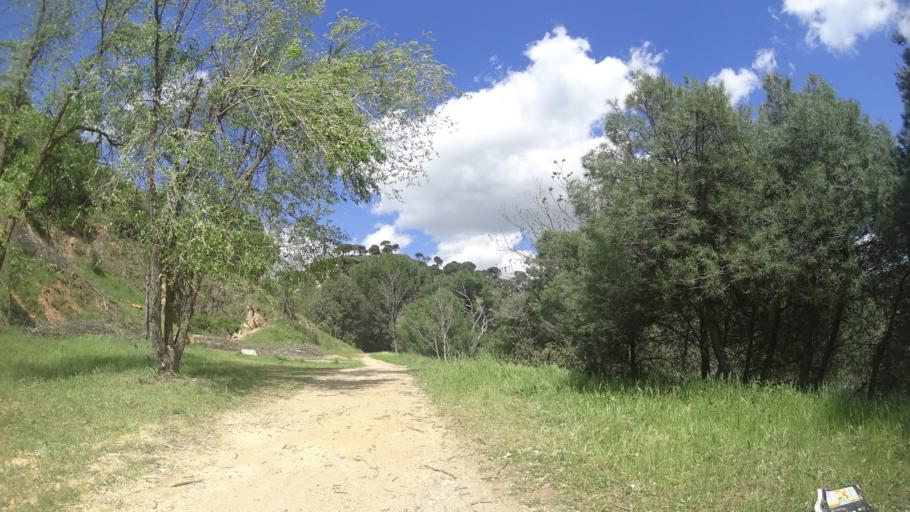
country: ES
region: Madrid
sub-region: Provincia de Madrid
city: Pelayos de la Presa
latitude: 40.3659
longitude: -4.3057
